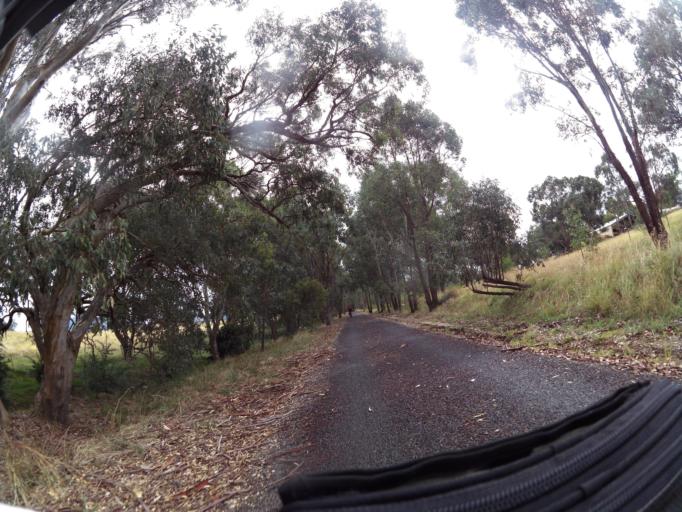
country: AU
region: New South Wales
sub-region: Albury Municipality
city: East Albury
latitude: -36.1435
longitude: 147.0010
